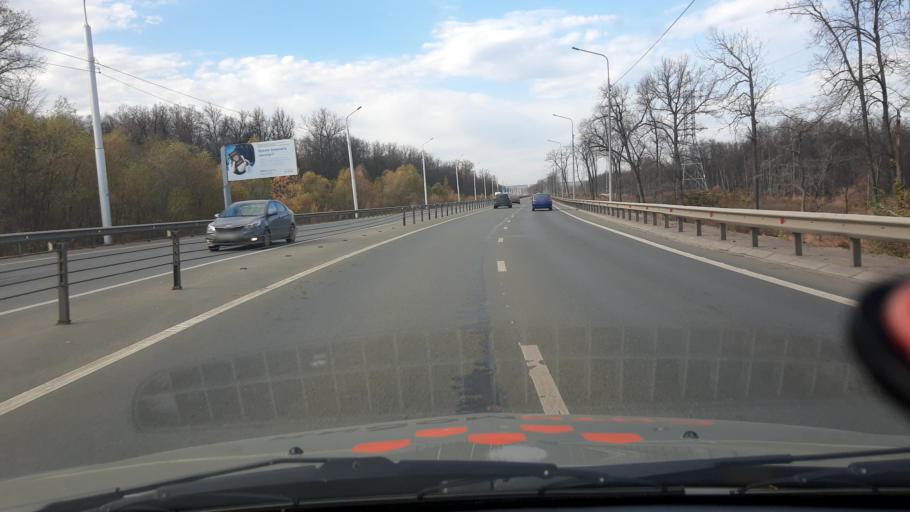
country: RU
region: Bashkortostan
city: Ufa
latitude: 54.6974
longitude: 55.8925
